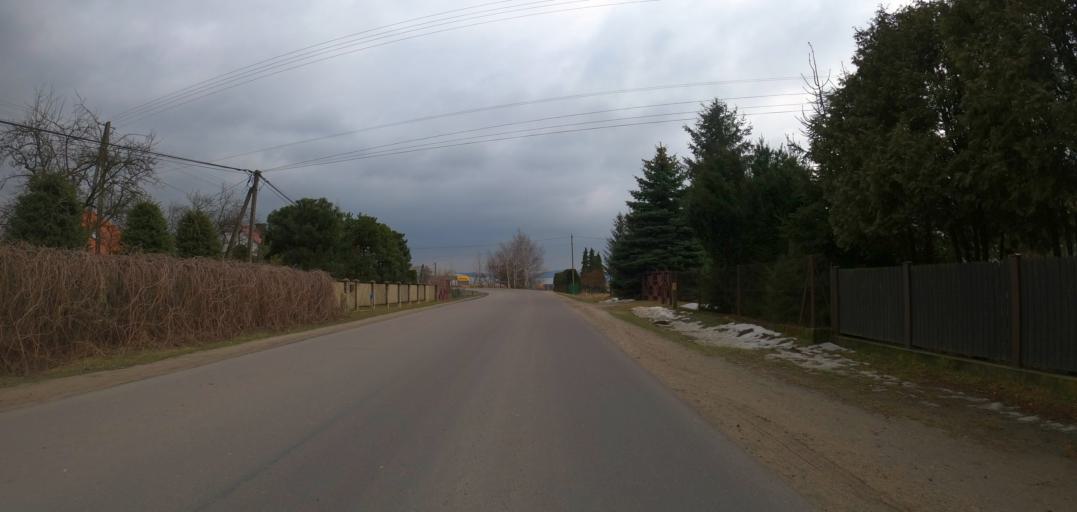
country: PL
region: Subcarpathian Voivodeship
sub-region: Powiat debicki
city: Pilzno
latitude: 49.9882
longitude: 21.3139
